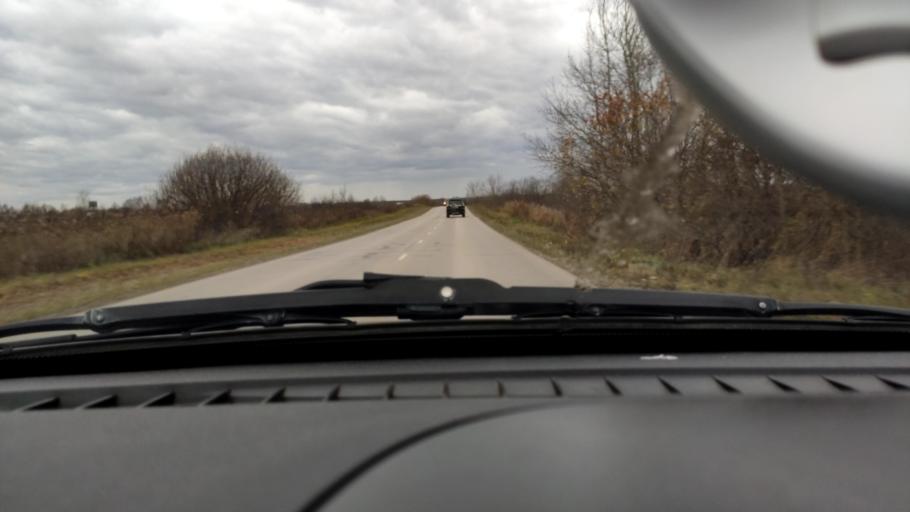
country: RU
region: Perm
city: Kondratovo
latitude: 58.0013
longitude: 56.0687
